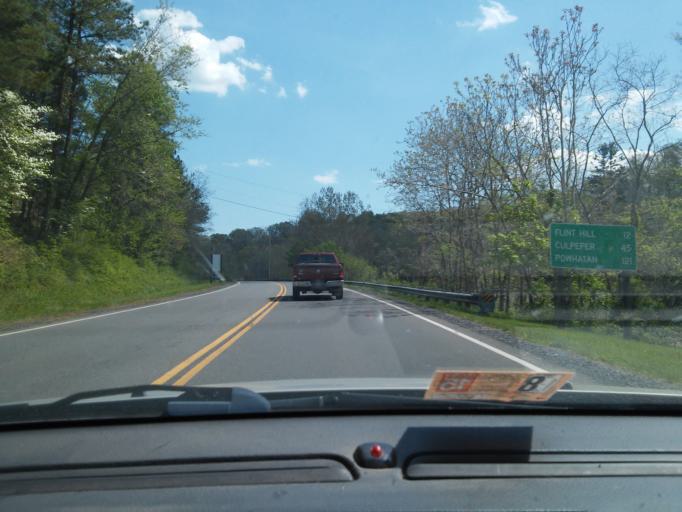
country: US
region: Virginia
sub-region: Warren County
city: Front Royal
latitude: 38.9039
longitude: -78.1849
